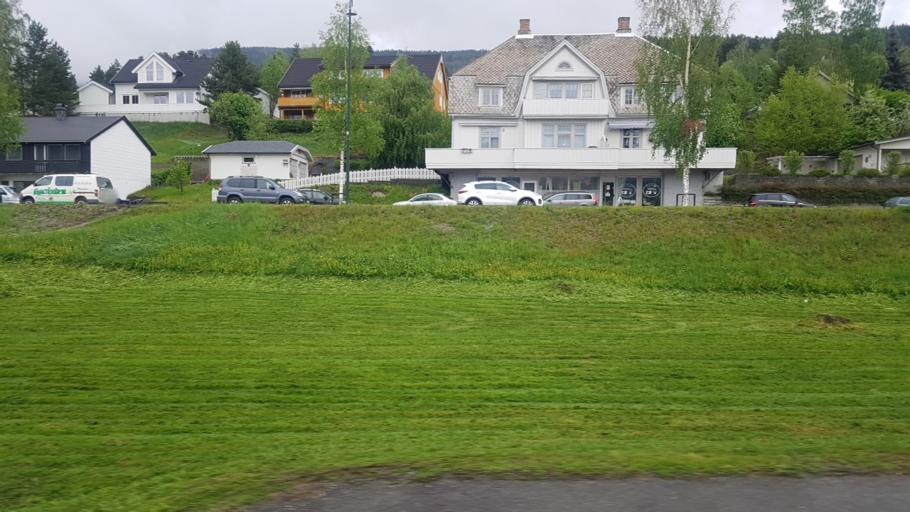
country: NO
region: Oppland
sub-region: Nord-Fron
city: Vinstra
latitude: 61.6021
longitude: 9.7392
